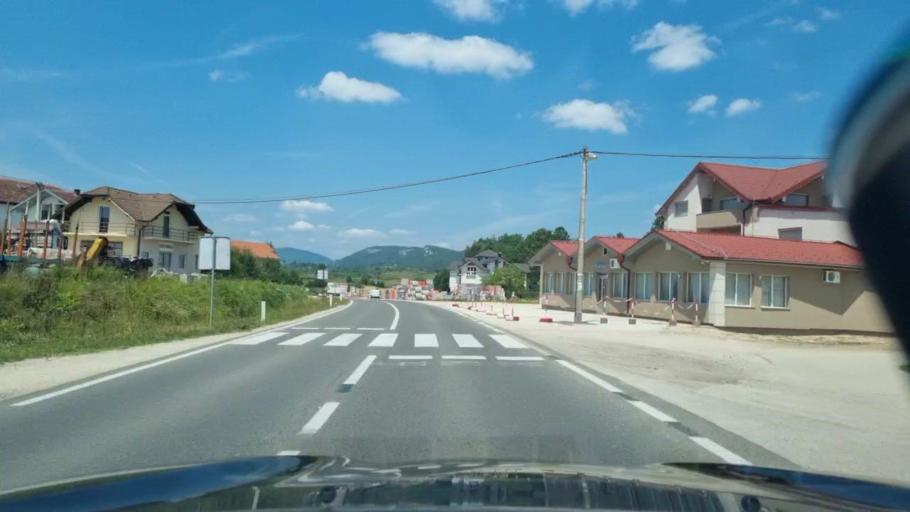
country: BA
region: Federation of Bosnia and Herzegovina
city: Velagici
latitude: 44.5497
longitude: 16.7483
